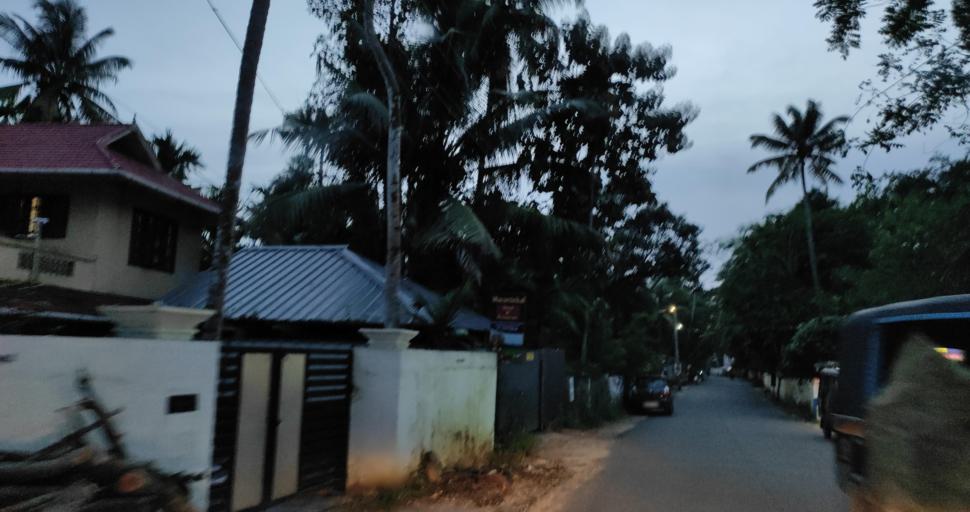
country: IN
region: Kerala
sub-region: Alappuzha
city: Vayalar
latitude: 9.7037
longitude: 76.3120
